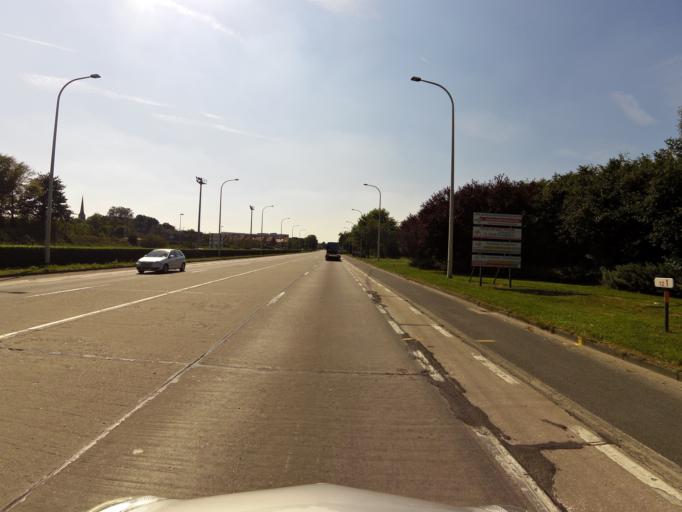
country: BE
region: Flanders
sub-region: Provincie West-Vlaanderen
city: Tielt
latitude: 51.0054
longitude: 3.3293
